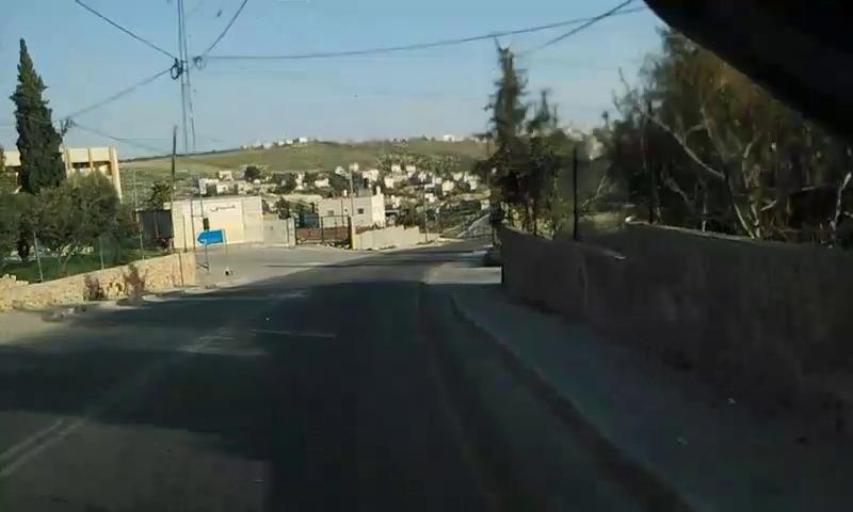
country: PS
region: West Bank
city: Jannatah
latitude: 31.6493
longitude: 35.2167
